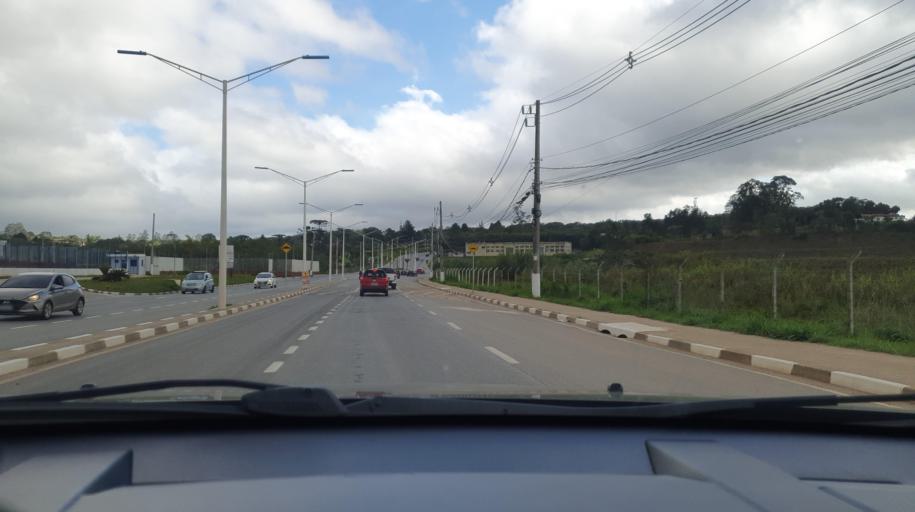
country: BR
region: Sao Paulo
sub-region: Vargem Grande Paulista
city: Vargem Grande Paulista
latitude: -23.6513
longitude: -46.9960
